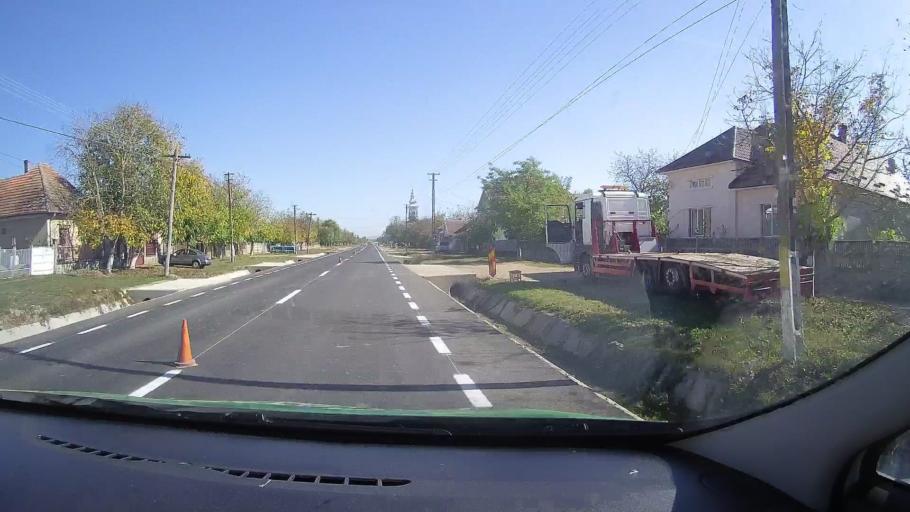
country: RO
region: Satu Mare
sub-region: Oras Ardud
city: Madaras
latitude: 47.6846
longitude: 22.8572
